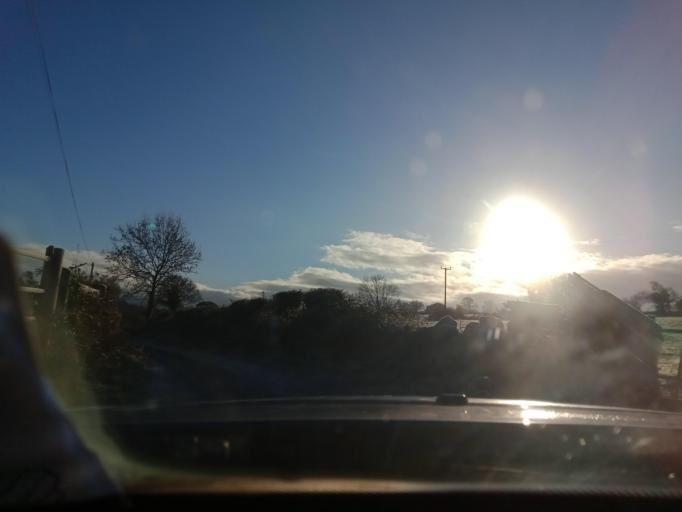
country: IE
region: Leinster
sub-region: Kilkenny
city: Graiguenamanagh
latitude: 52.5984
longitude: -6.9520
